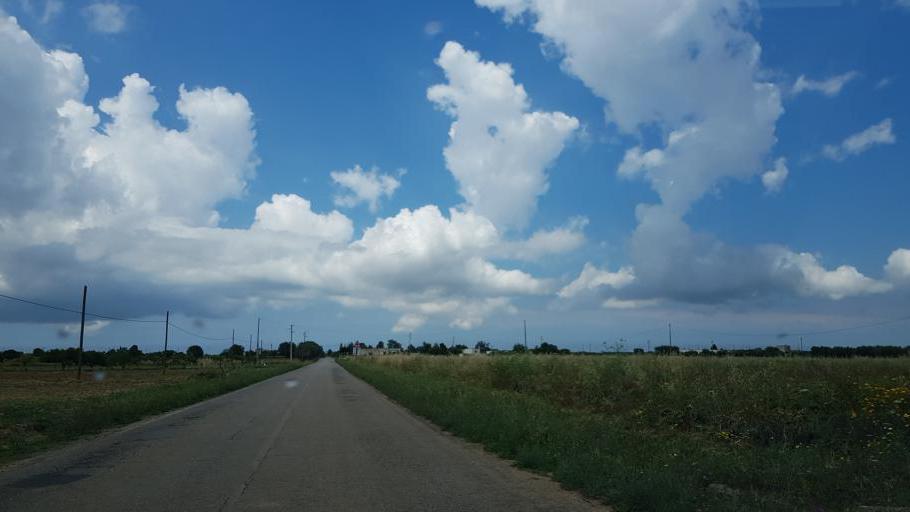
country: IT
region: Apulia
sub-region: Provincia di Brindisi
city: Tuturano
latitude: 40.5261
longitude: 17.9409
